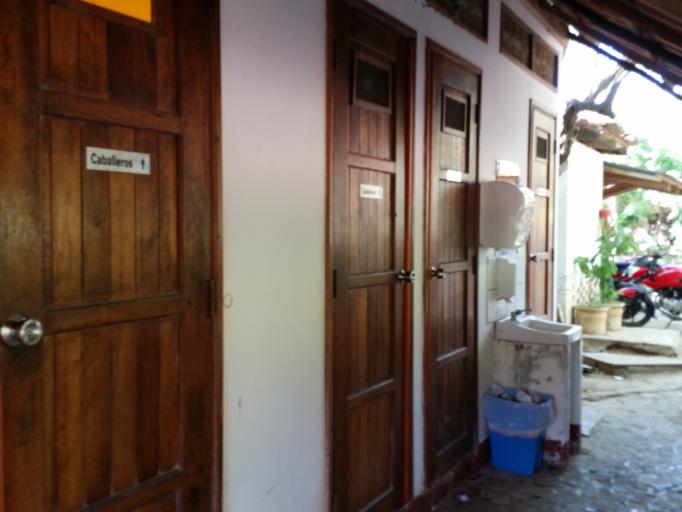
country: NI
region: Rivas
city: San Juan del Sur
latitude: 11.1588
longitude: -85.8022
